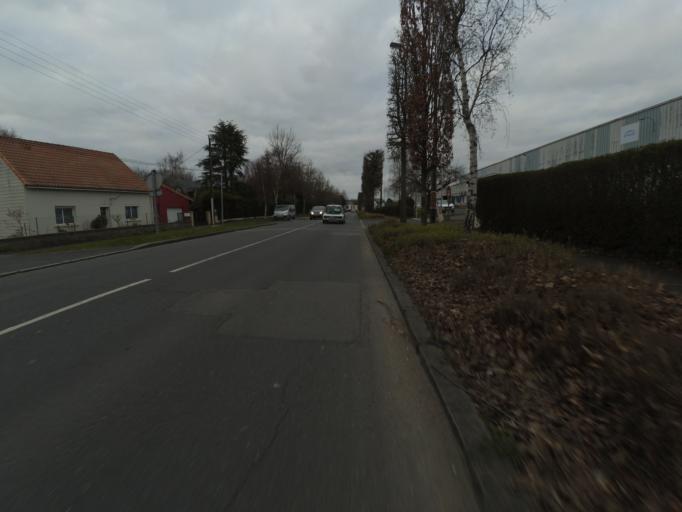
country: FR
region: Pays de la Loire
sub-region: Departement de la Loire-Atlantique
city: Sainte-Luce-sur-Loire
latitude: 47.2729
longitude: -1.4990
